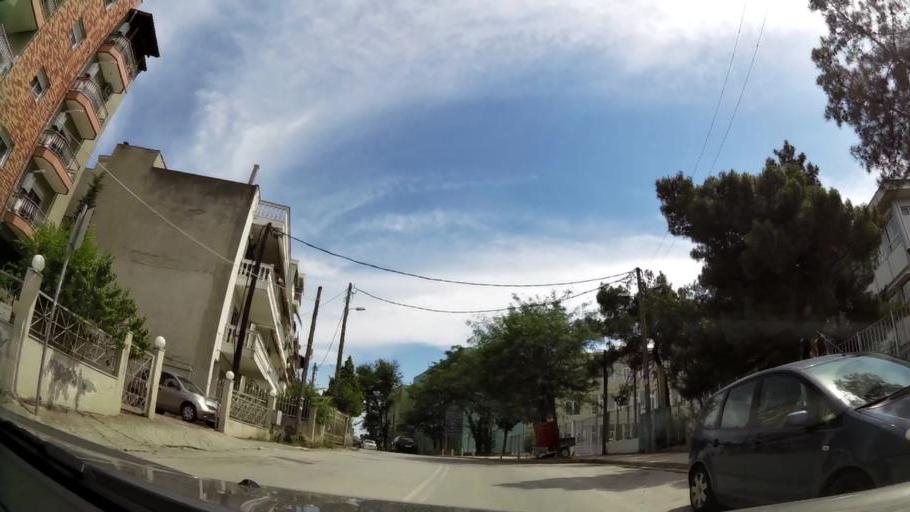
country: GR
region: Central Macedonia
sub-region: Nomos Thessalonikis
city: Pylaia
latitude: 40.5963
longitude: 22.9747
